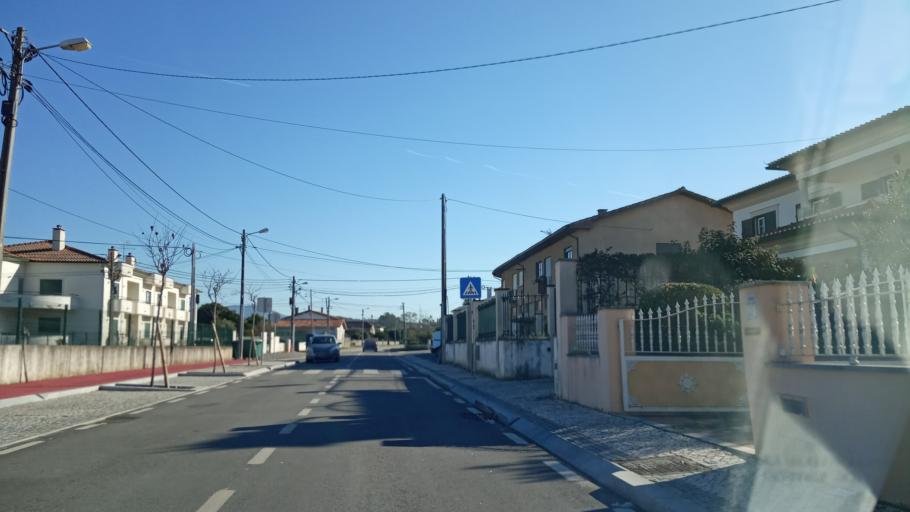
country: PT
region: Aveiro
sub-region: Anadia
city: Anadia
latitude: 40.4311
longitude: -8.4301
